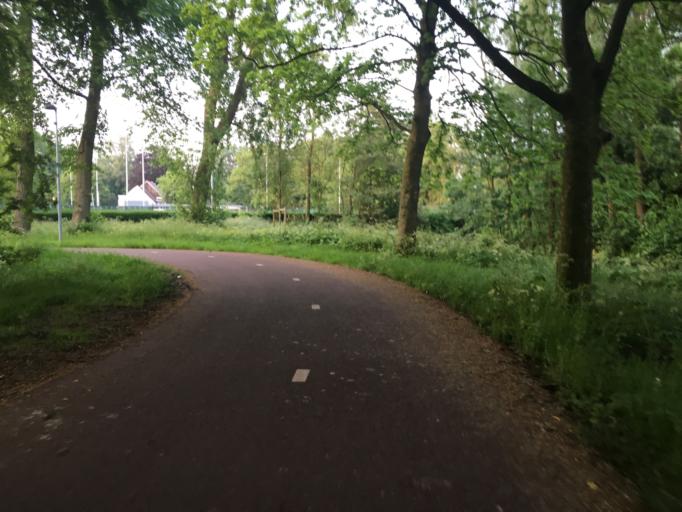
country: NL
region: South Holland
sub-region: Gemeente Schiedam
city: Schiedam
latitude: 51.9159
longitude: 4.3752
